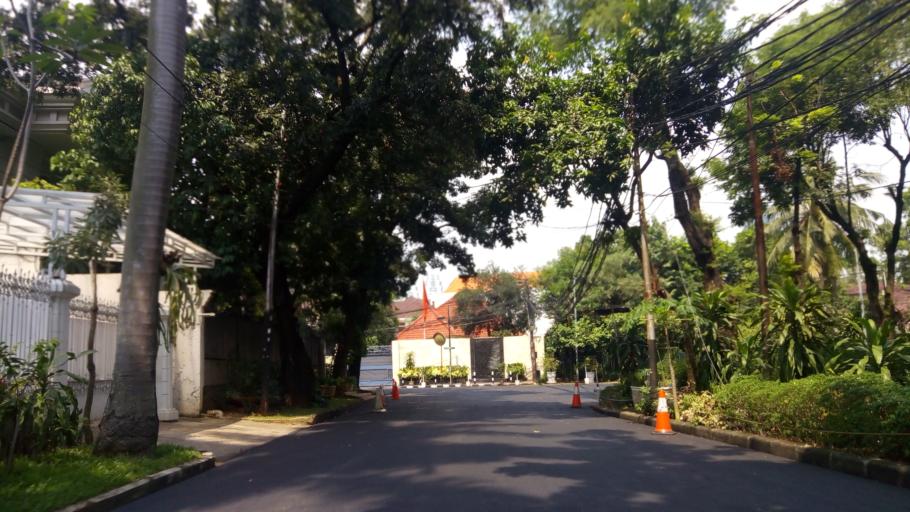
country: ID
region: Jakarta Raya
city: Jakarta
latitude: -6.1977
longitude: 106.8276
